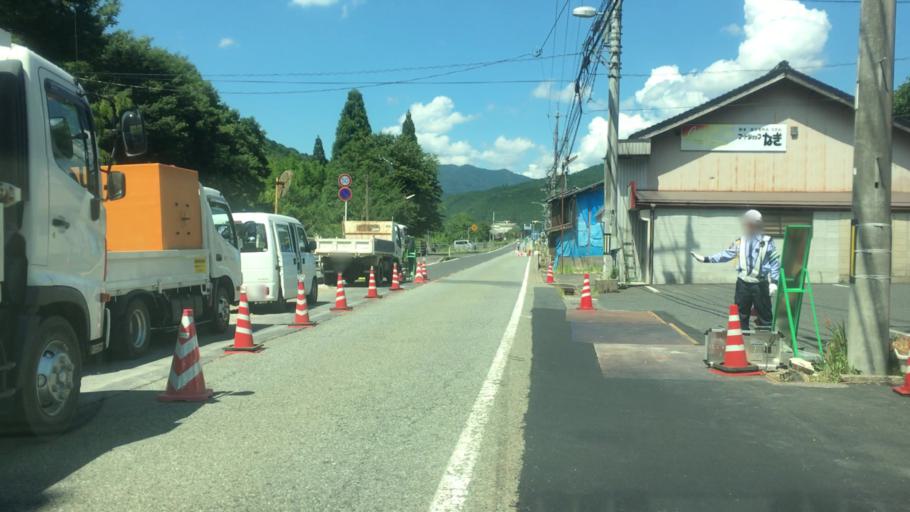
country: JP
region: Okayama
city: Tsuyama
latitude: 35.2170
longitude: 134.2198
